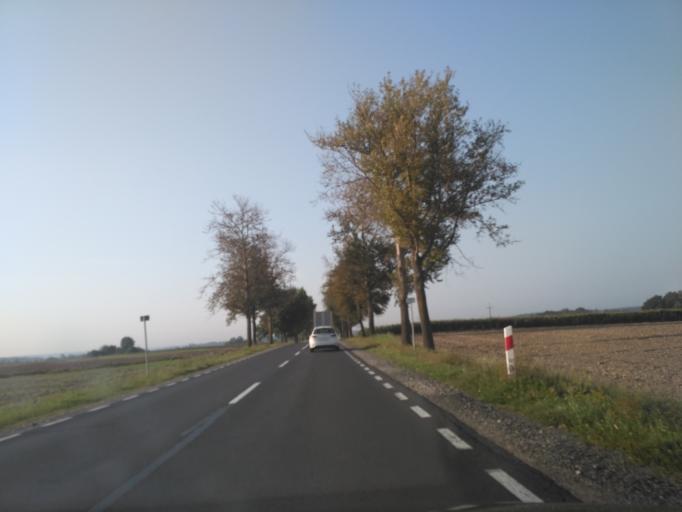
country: PL
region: Lublin Voivodeship
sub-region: Powiat krasnicki
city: Szastarka
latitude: 50.8128
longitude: 22.3193
